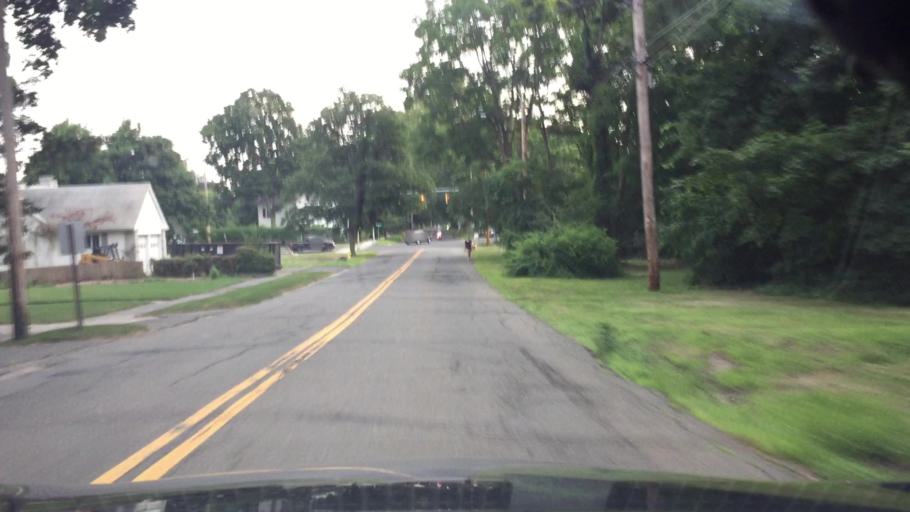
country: US
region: Connecticut
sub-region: Fairfield County
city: Stratford
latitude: 41.1878
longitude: -73.1279
